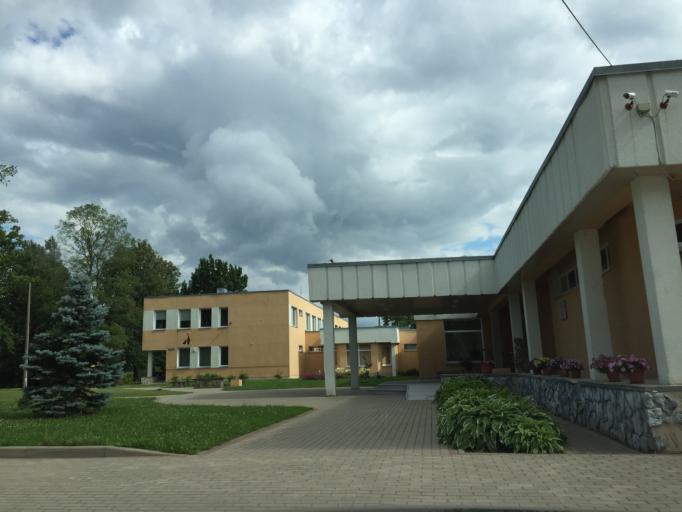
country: LV
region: Malpils
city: Malpils
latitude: 56.8581
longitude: 25.0207
